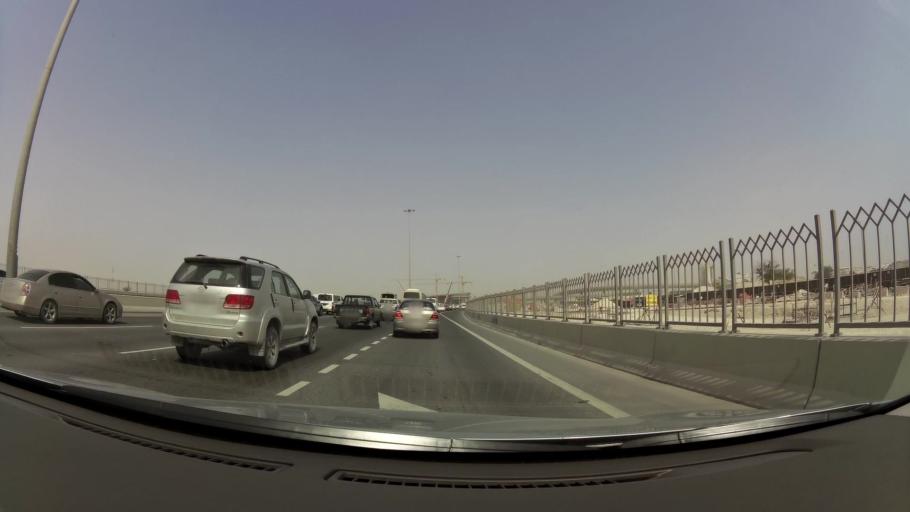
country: QA
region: Baladiyat ad Dawhah
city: Doha
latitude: 25.2902
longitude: 51.4780
